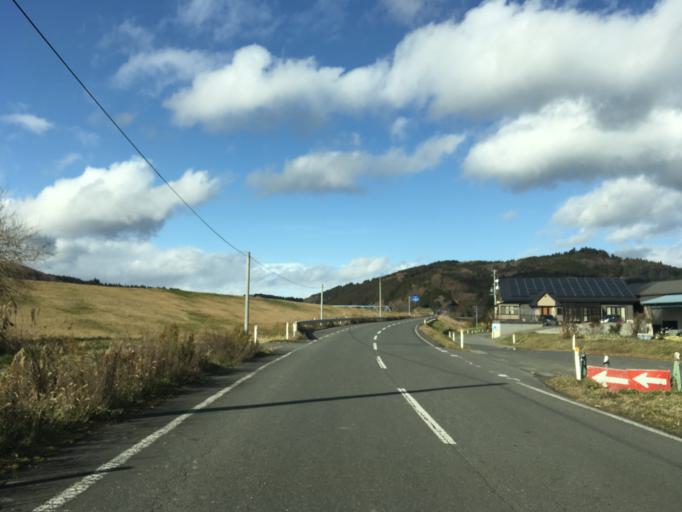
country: JP
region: Iwate
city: Ichinoseki
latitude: 38.8394
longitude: 141.2656
